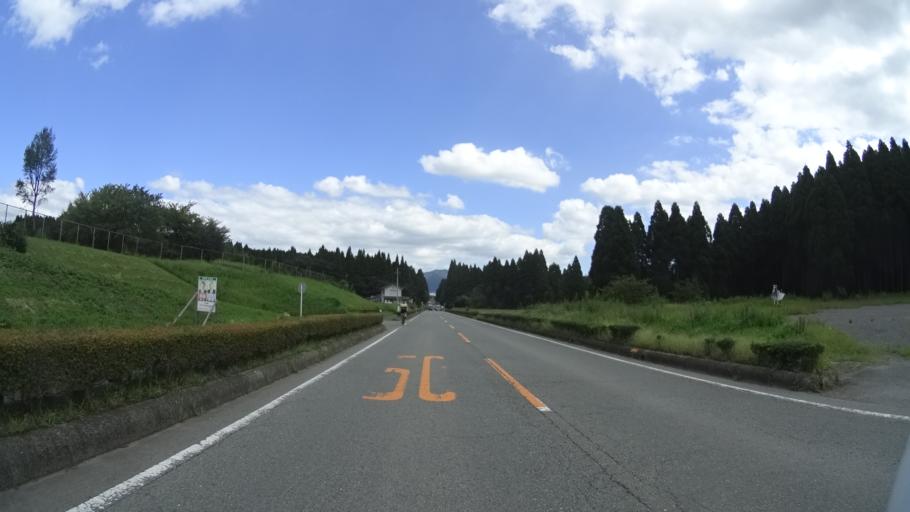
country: JP
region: Kumamoto
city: Aso
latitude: 32.8315
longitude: 131.0822
